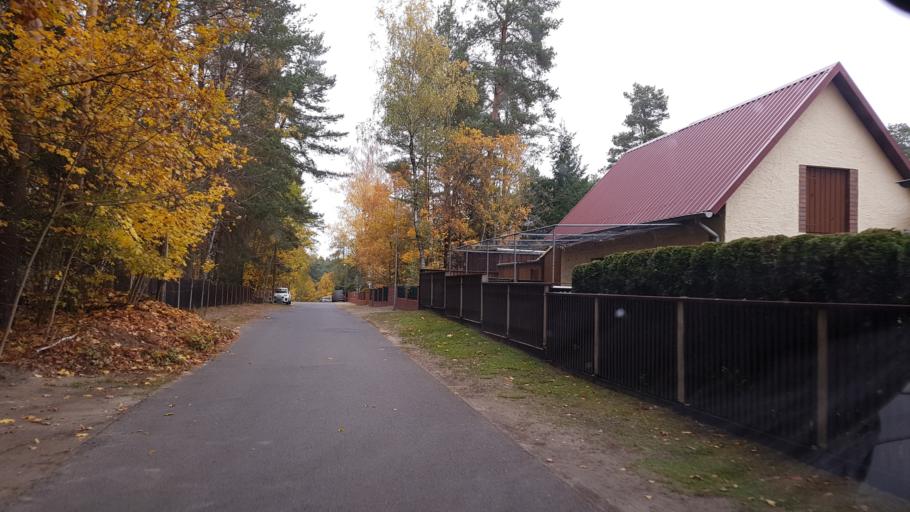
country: DE
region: Brandenburg
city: Crinitz
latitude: 51.7376
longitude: 13.7522
